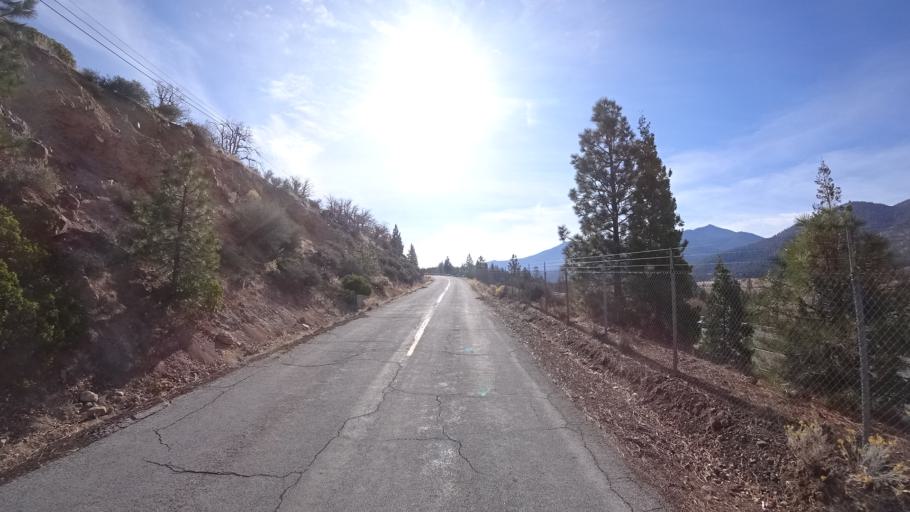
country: US
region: California
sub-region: Siskiyou County
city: Weed
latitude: 41.4344
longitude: -122.4295
